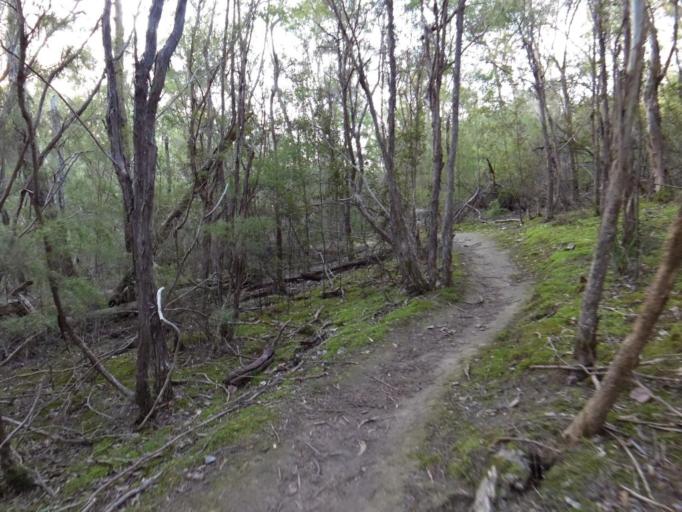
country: AU
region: Victoria
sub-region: Nillumbik
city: North Warrandyte
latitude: -37.7251
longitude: 145.2368
